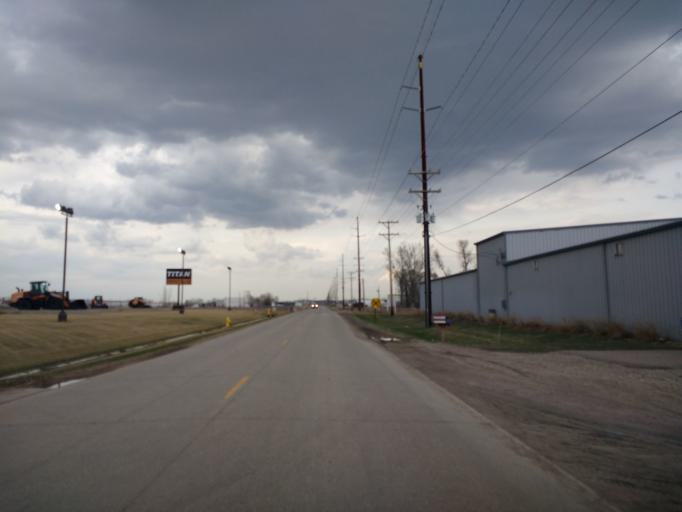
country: US
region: Iowa
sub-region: Woodbury County
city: Sergeant Bluff
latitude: 42.4082
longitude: -96.3701
